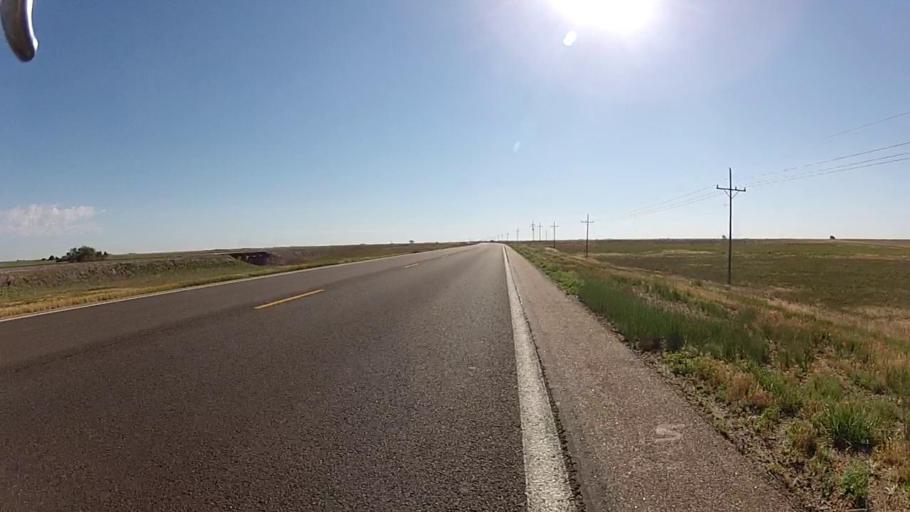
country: US
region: Kansas
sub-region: Haskell County
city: Sublette
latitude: 37.5557
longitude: -100.5827
